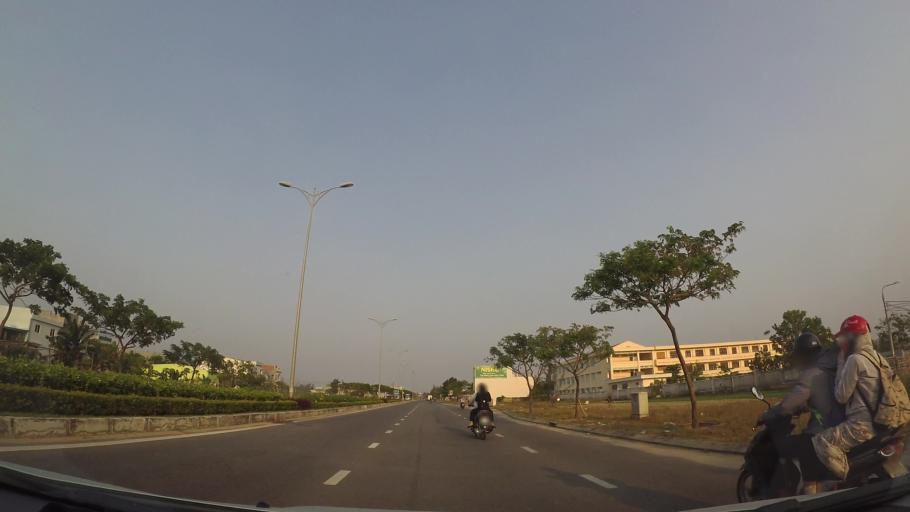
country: VN
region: Da Nang
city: Ngu Hanh Son
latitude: 15.9831
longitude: 108.2487
